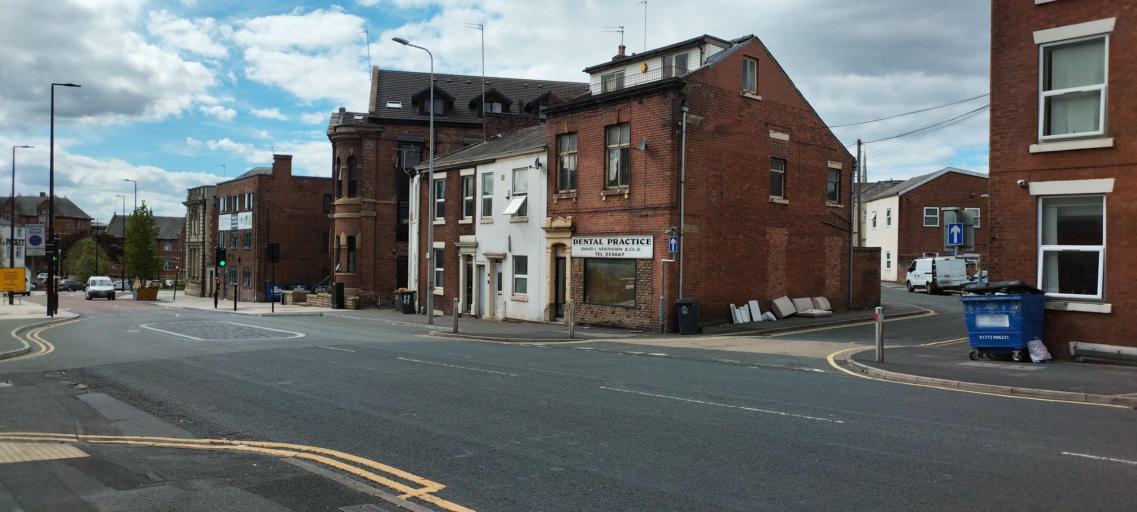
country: GB
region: England
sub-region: Lancashire
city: Preston
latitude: 53.7633
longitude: -2.7052
